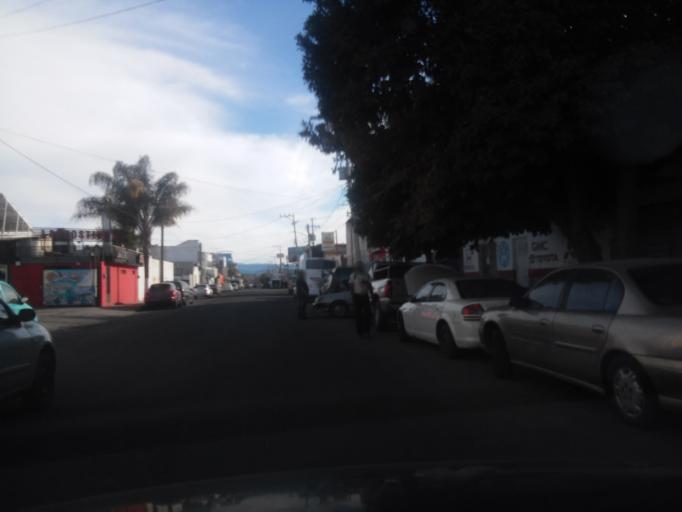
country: MX
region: Durango
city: Victoria de Durango
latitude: 24.0270
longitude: -104.6545
